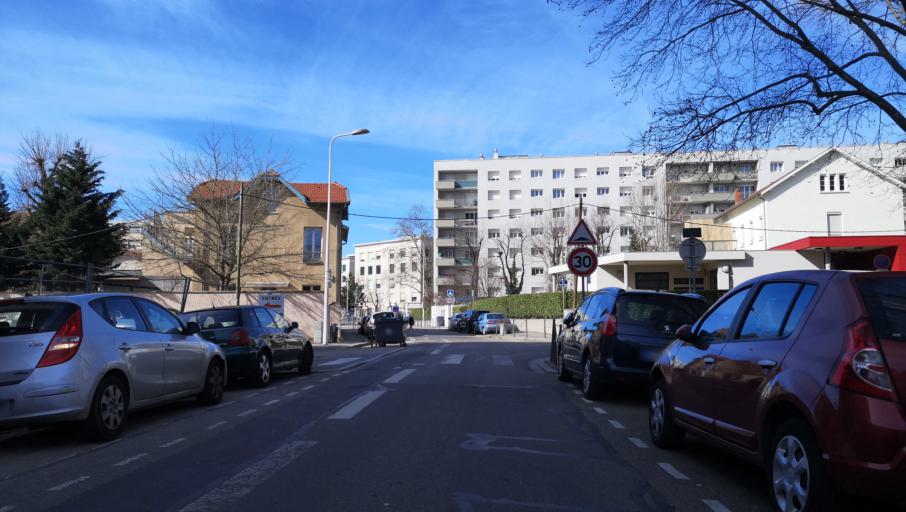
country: FR
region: Rhone-Alpes
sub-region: Departement du Rhone
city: Villeurbanne
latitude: 45.7395
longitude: 4.8827
